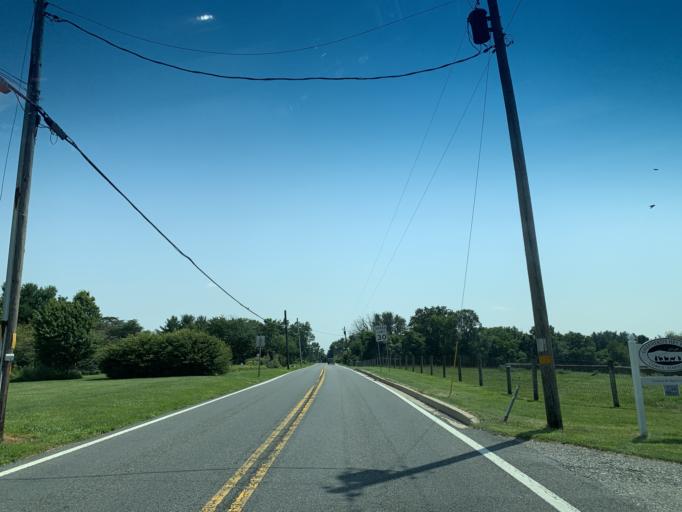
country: US
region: Maryland
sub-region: Montgomery County
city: Clarksburg
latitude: 39.2503
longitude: -77.3476
